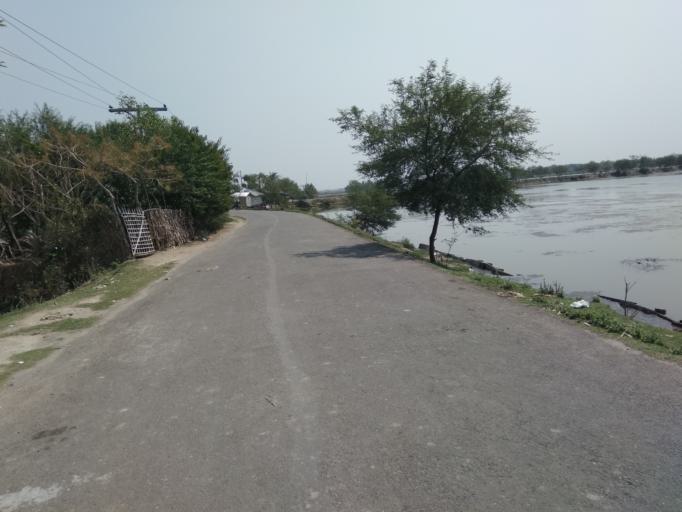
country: IN
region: West Bengal
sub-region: North 24 Parganas
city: Taki
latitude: 22.4015
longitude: 89.2132
